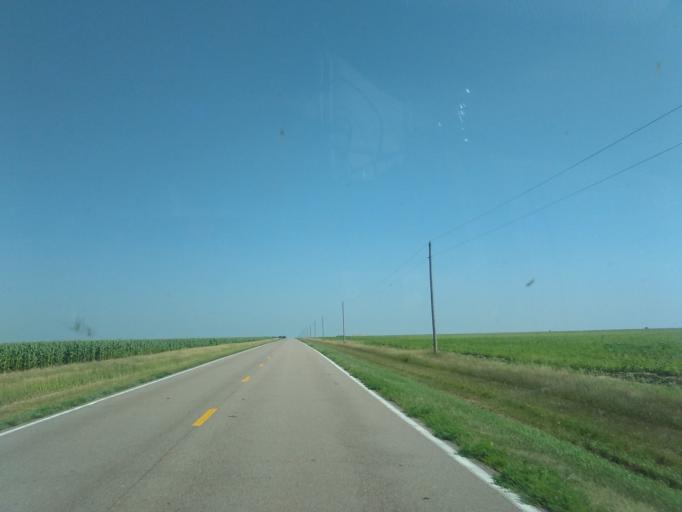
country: US
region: Nebraska
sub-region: Dundy County
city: Benkelman
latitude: 39.8315
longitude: -101.5411
